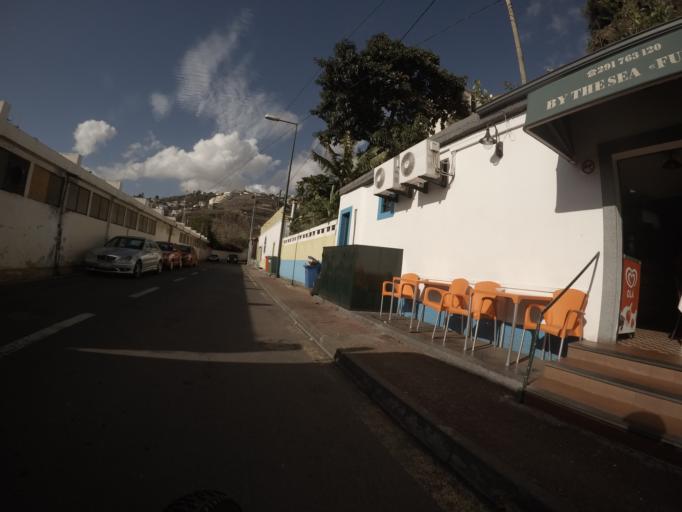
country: PT
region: Madeira
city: Camara de Lobos
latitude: 32.6397
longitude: -16.9504
